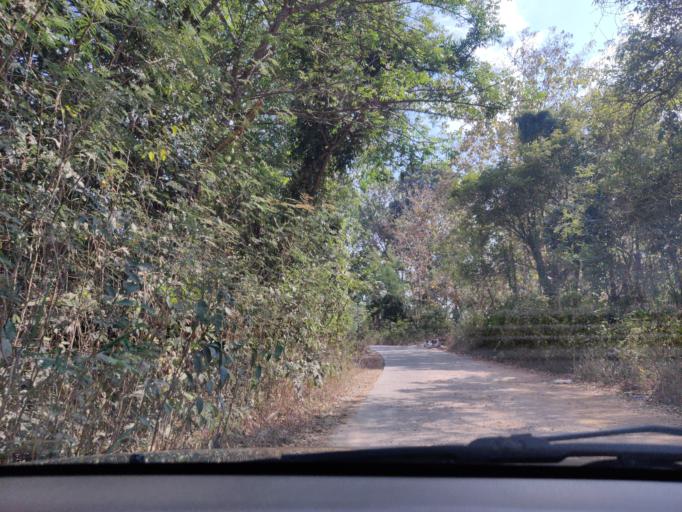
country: TH
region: Sisaket
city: Si Sa Ket
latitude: 15.0728
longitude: 104.3493
